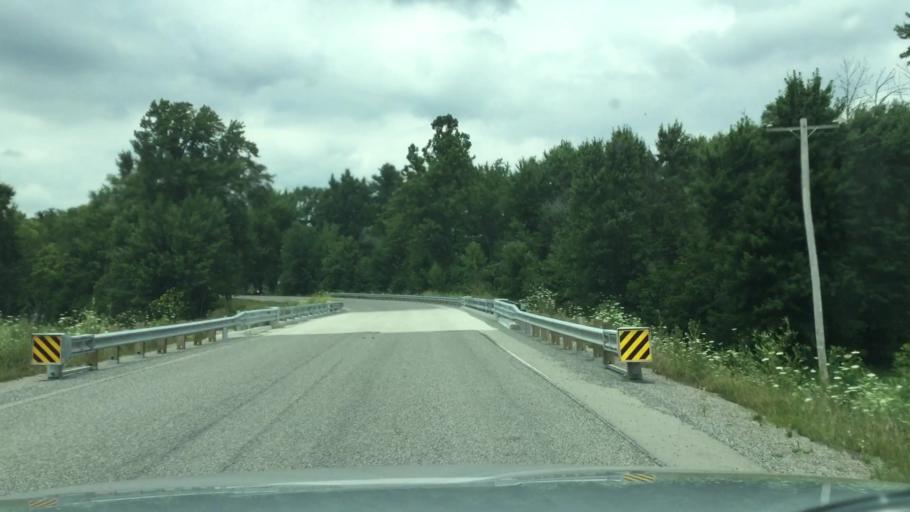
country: US
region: Michigan
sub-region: Saginaw County
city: Burt
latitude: 43.2772
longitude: -83.8853
